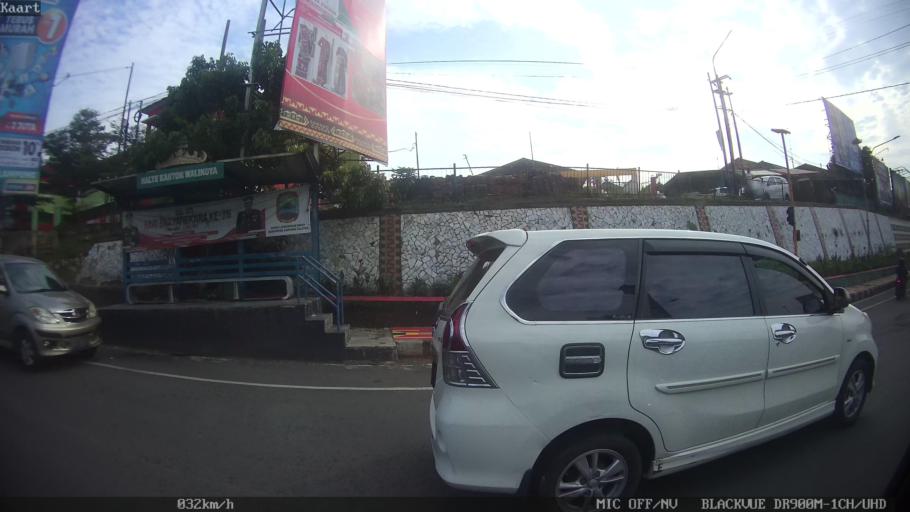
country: ID
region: Lampung
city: Bandarlampung
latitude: -5.4280
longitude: 105.2606
